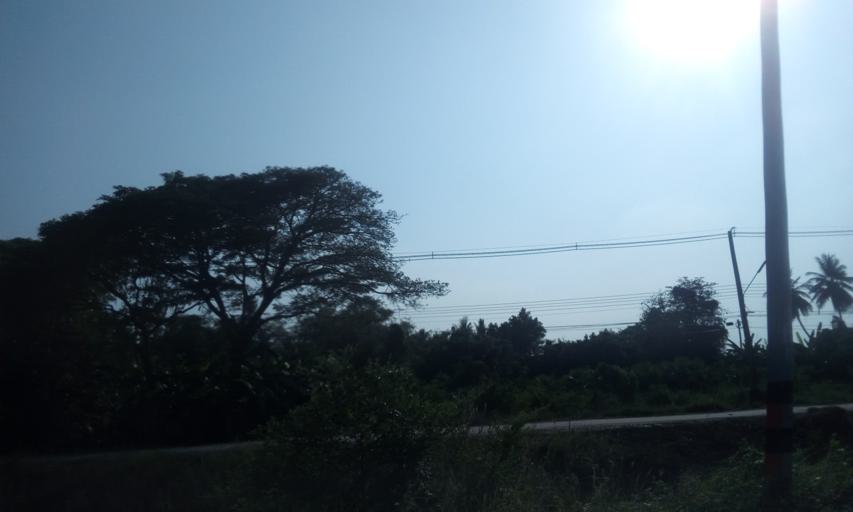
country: TH
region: Sing Buri
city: Sing Buri
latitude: 14.8478
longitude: 100.4187
